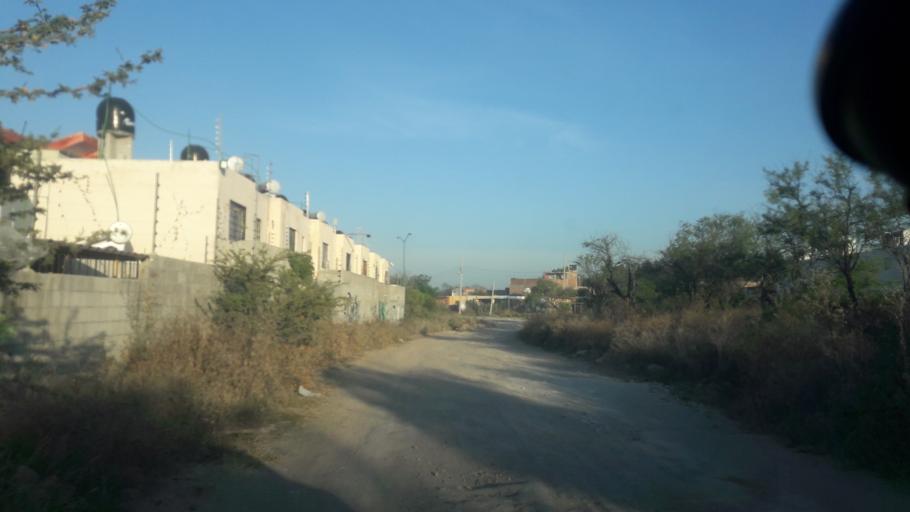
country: MX
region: Guanajuato
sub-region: Leon
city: Medina
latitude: 21.1654
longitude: -101.6350
